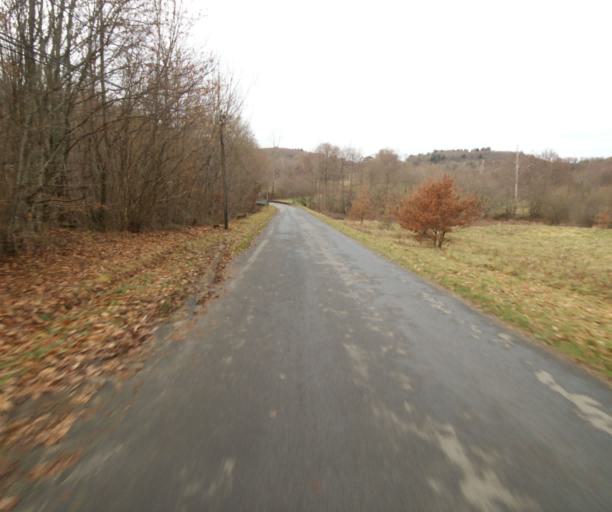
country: FR
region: Limousin
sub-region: Departement de la Correze
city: Chameyrat
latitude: 45.2362
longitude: 1.6890
